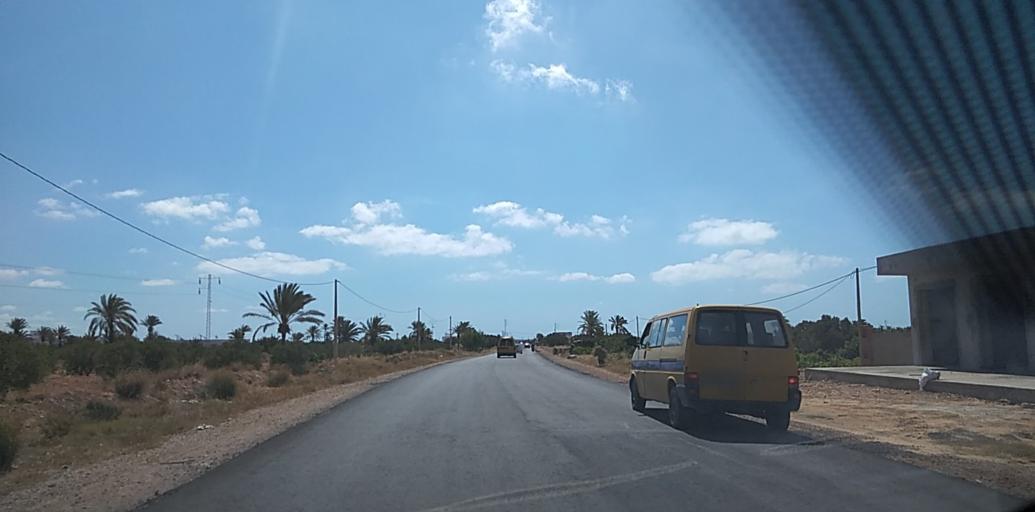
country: TN
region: Safaqis
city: Al Qarmadah
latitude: 34.6576
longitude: 11.0829
